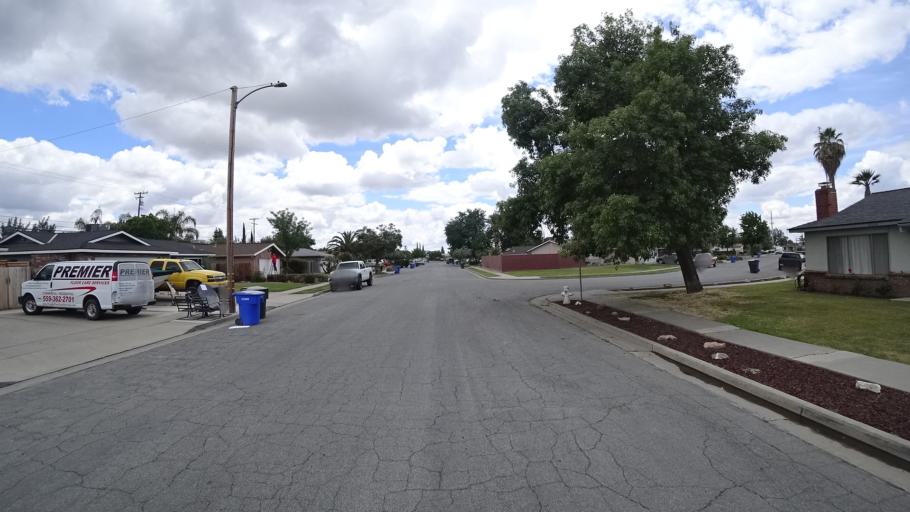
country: US
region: California
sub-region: Kings County
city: Hanford
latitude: 36.3488
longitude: -119.6378
